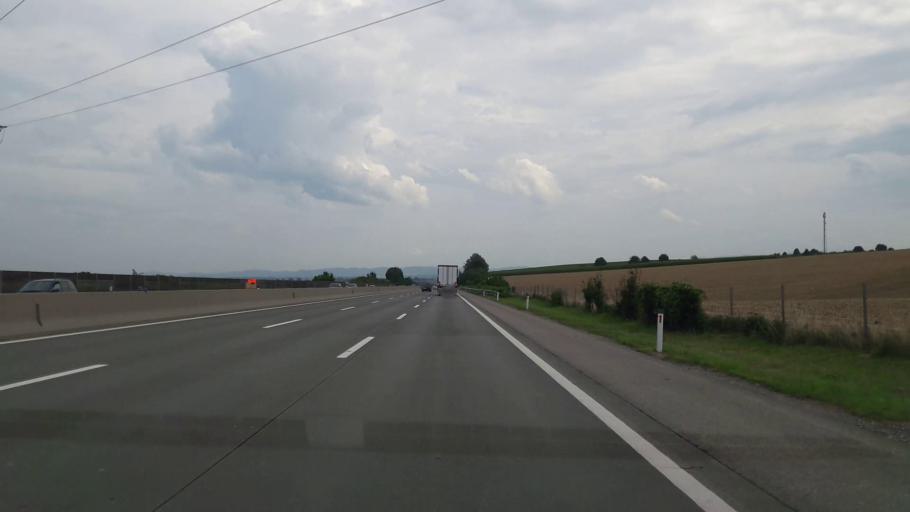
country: AT
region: Lower Austria
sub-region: Politischer Bezirk Sankt Polten
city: Haunoldstein
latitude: 48.1778
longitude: 15.4572
